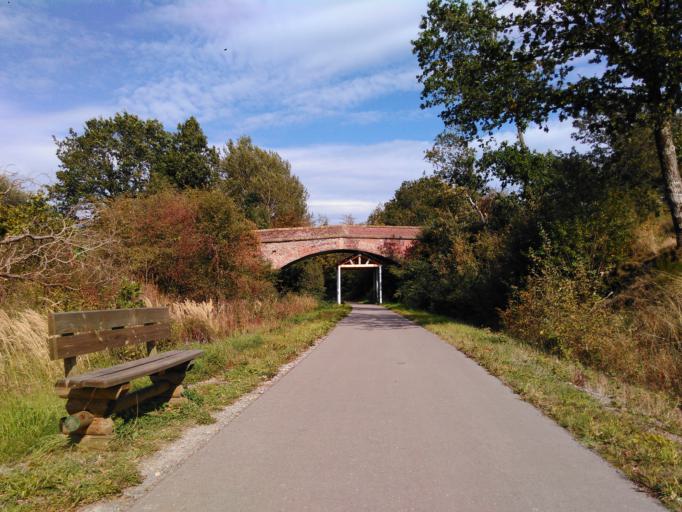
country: BE
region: Wallonia
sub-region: Province du Luxembourg
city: Gouvy
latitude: 50.1598
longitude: 5.9469
